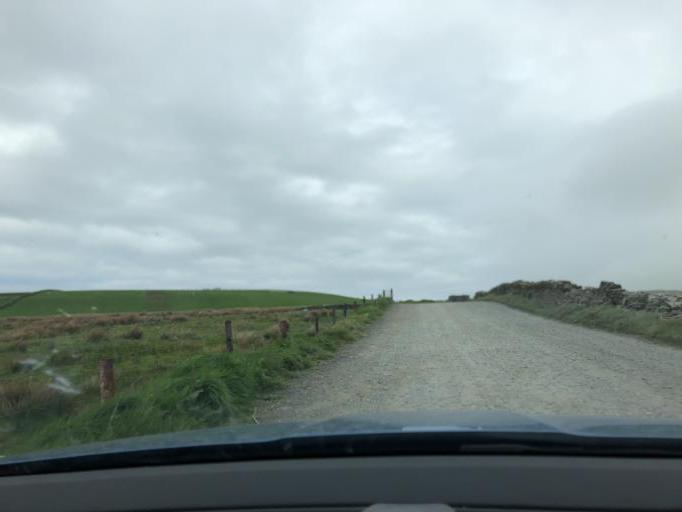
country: IE
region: Munster
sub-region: An Clar
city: Kilrush
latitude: 52.9612
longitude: -9.4311
